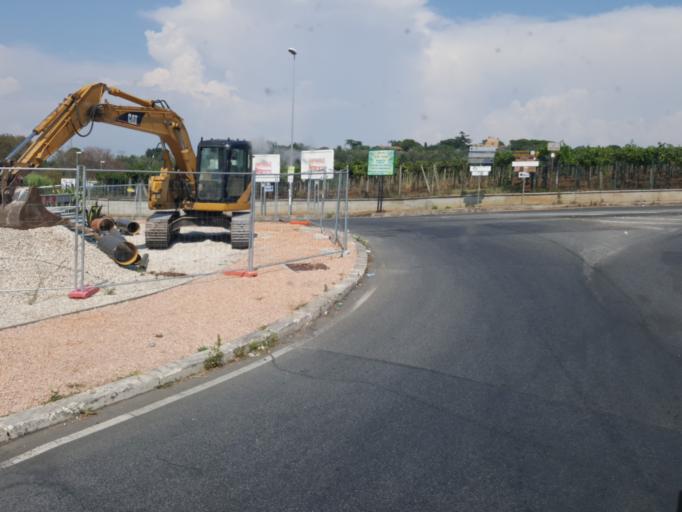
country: IT
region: Latium
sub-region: Citta metropolitana di Roma Capitale
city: Frascati
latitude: 41.8365
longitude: 12.6587
